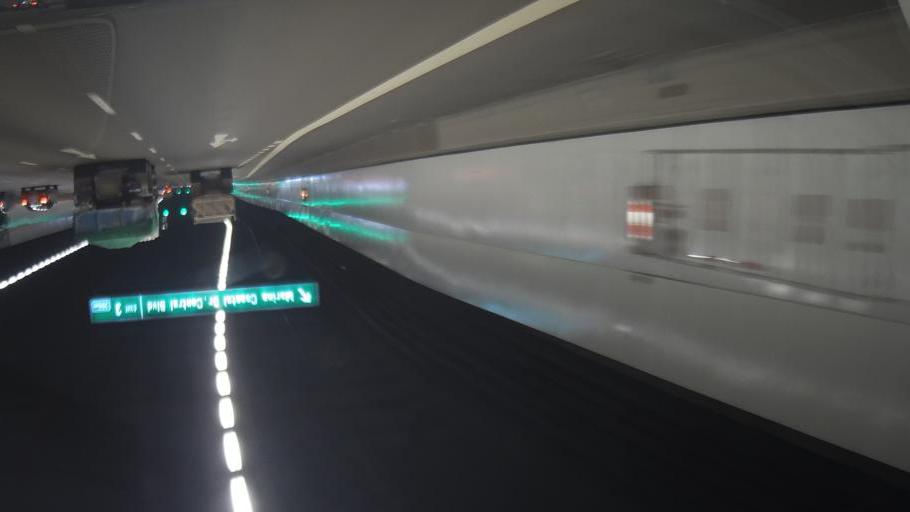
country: SG
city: Singapore
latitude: 1.2831
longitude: 103.8704
